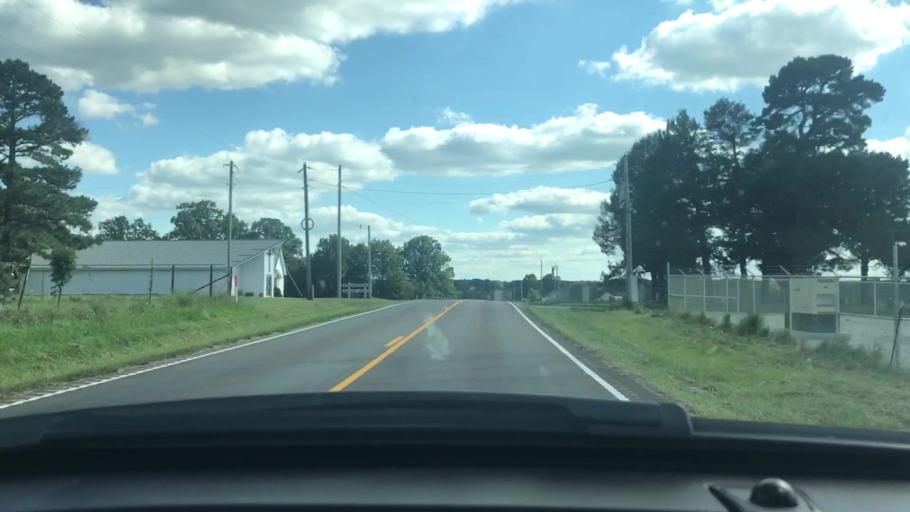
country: US
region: Missouri
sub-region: Wright County
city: Mountain Grove
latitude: 37.2474
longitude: -92.3003
